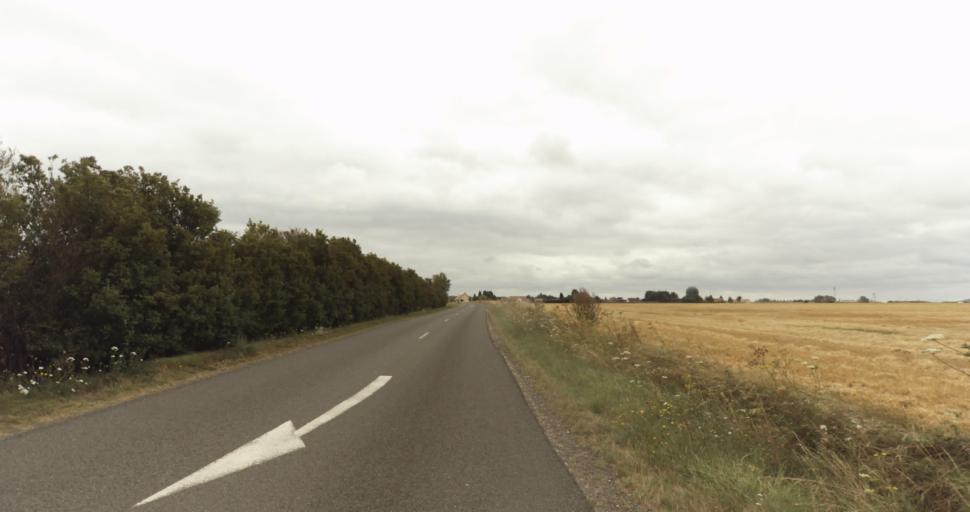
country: FR
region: Haute-Normandie
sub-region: Departement de l'Eure
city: Gravigny
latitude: 49.0377
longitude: 1.2392
